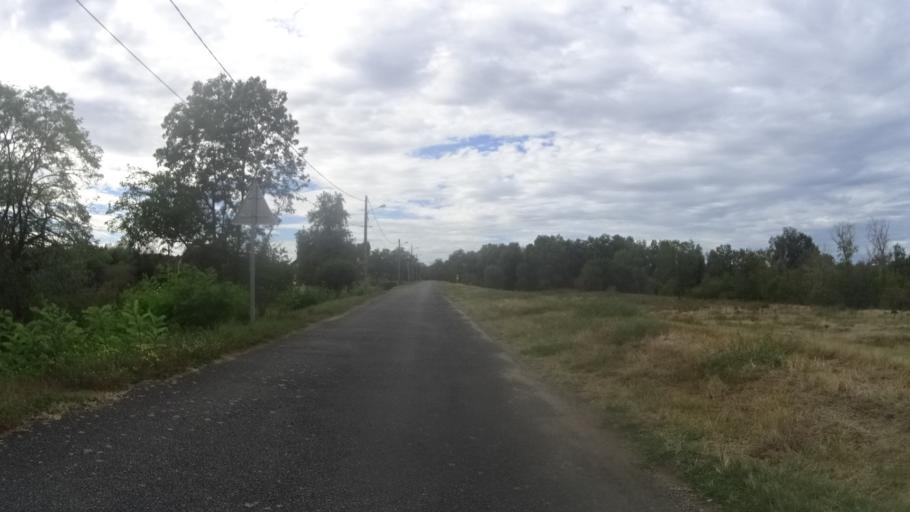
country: FR
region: Centre
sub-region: Departement du Cher
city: Cuffy
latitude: 46.9612
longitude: 3.0703
